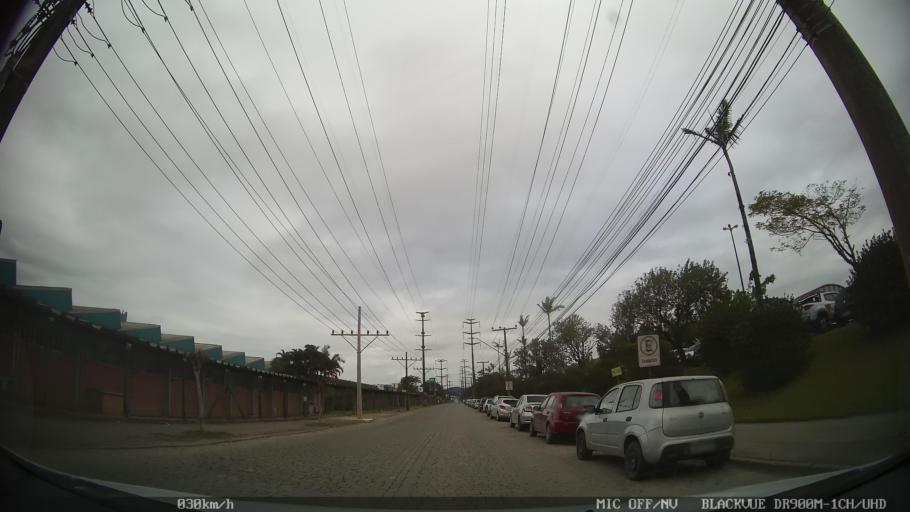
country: BR
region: Santa Catarina
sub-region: Joinville
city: Joinville
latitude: -26.2593
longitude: -48.8726
